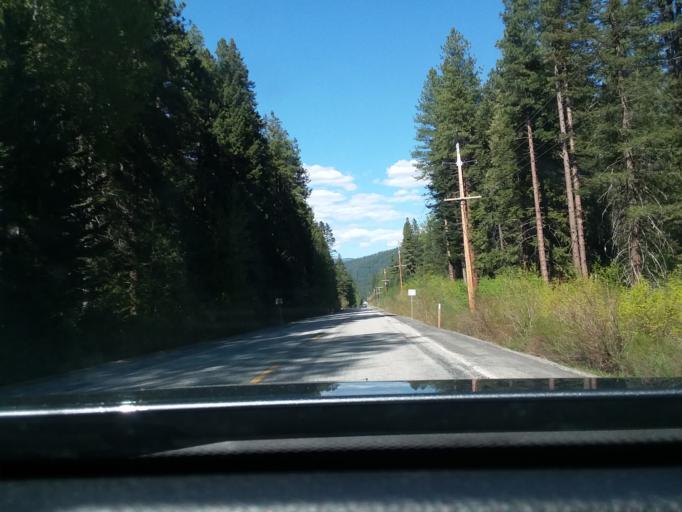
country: US
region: Washington
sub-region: Chelan County
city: Leavenworth
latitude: 47.7614
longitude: -120.7332
